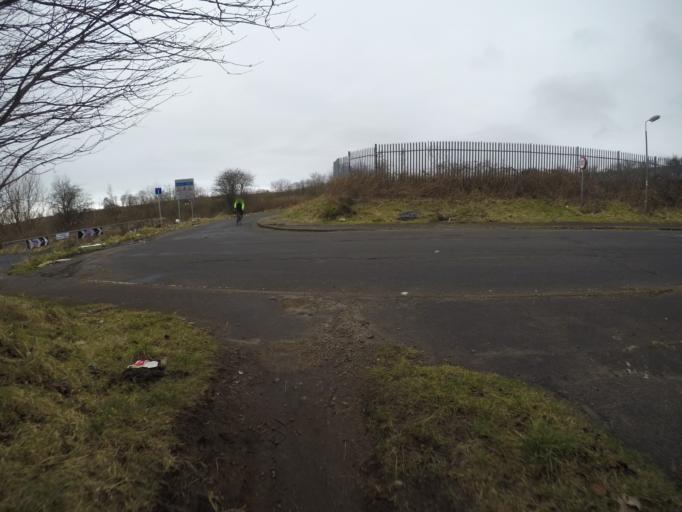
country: GB
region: Scotland
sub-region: North Ayrshire
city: Kilwinning
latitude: 55.6435
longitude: -4.6981
